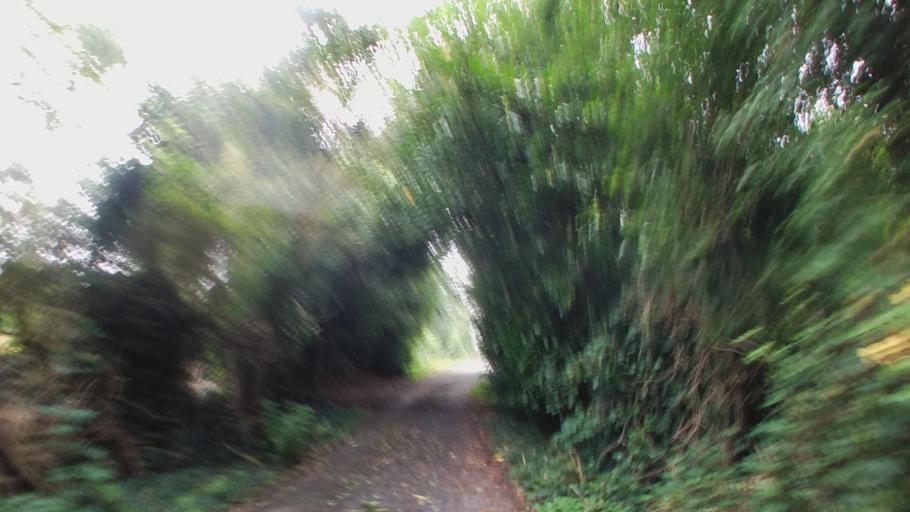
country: IE
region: Leinster
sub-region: Kilkenny
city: Kilkenny
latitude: 52.6993
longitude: -7.1997
